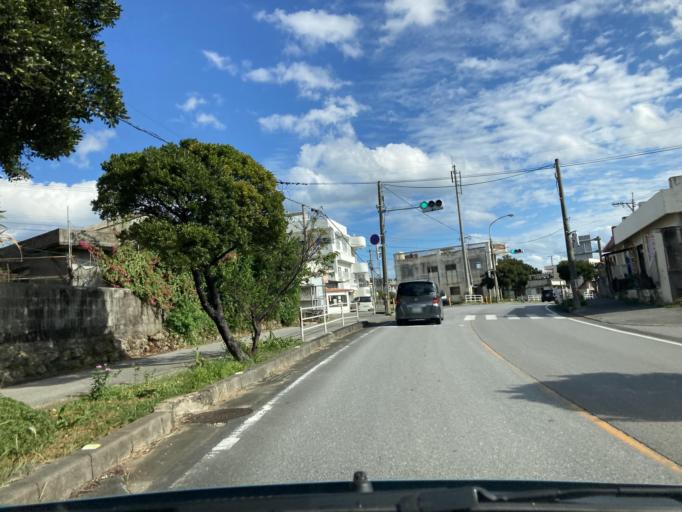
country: JP
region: Okinawa
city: Ishikawa
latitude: 26.4195
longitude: 127.8172
